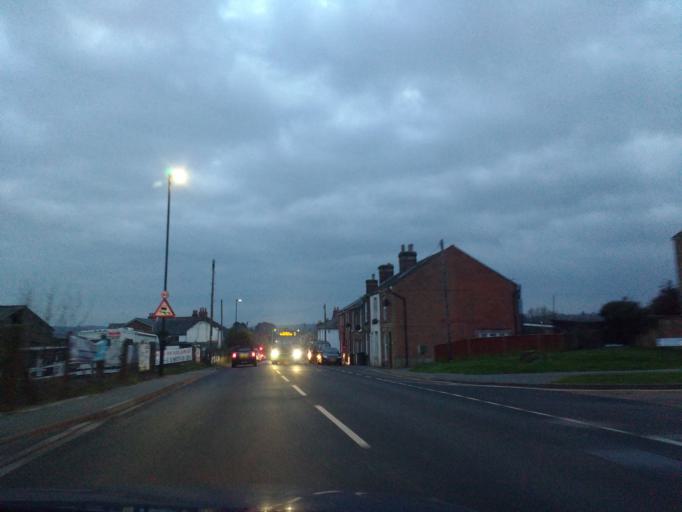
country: GB
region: England
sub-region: Isle of Wight
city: Northwood
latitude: 50.7204
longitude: -1.3042
